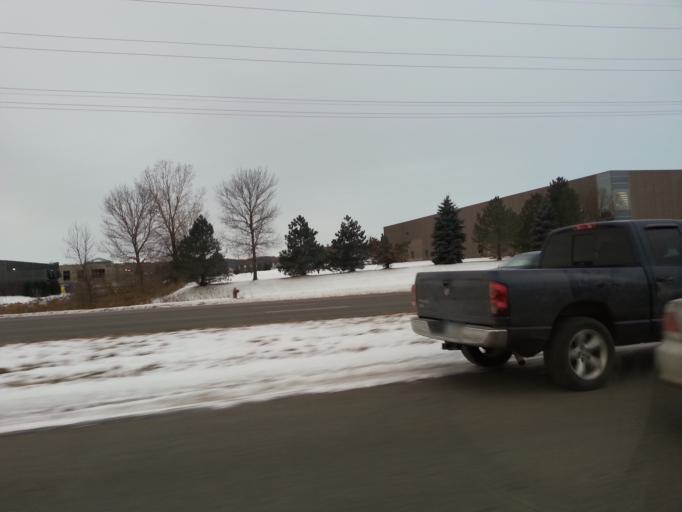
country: US
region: Minnesota
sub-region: Scott County
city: Savage
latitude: 44.7464
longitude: -93.3209
